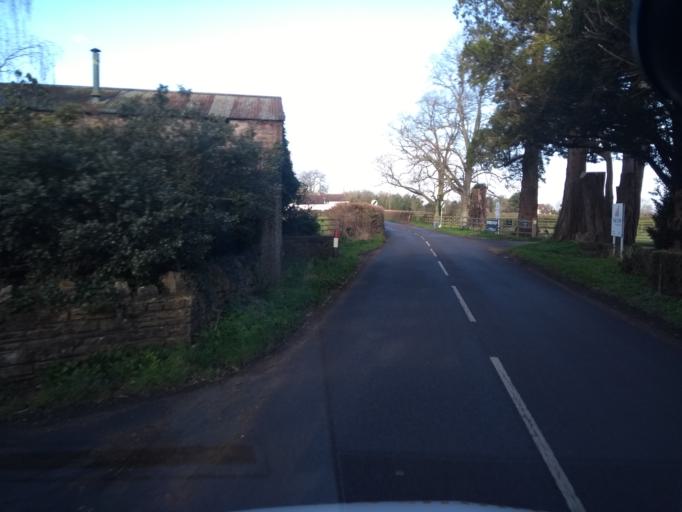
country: GB
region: England
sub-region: Somerset
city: Woolavington
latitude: 51.1563
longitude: -2.8998
